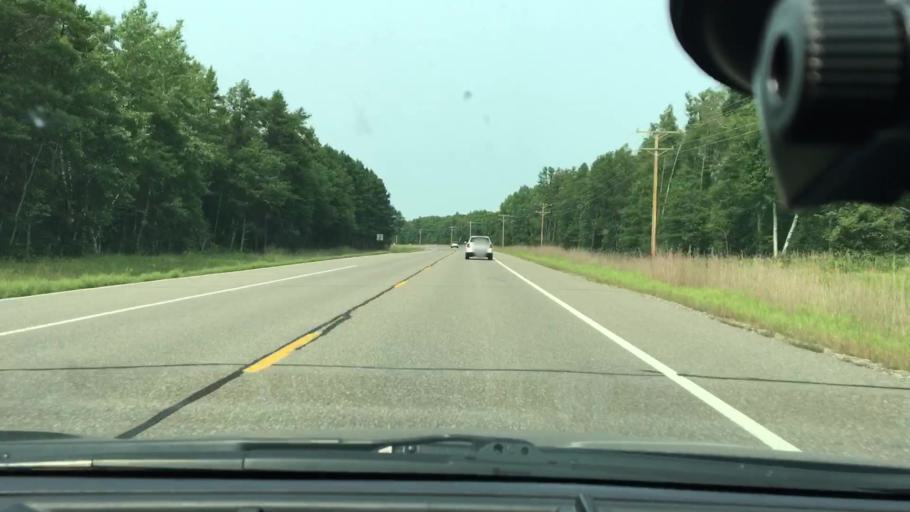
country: US
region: Minnesota
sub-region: Crow Wing County
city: Cross Lake
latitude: 46.5991
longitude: -94.1309
